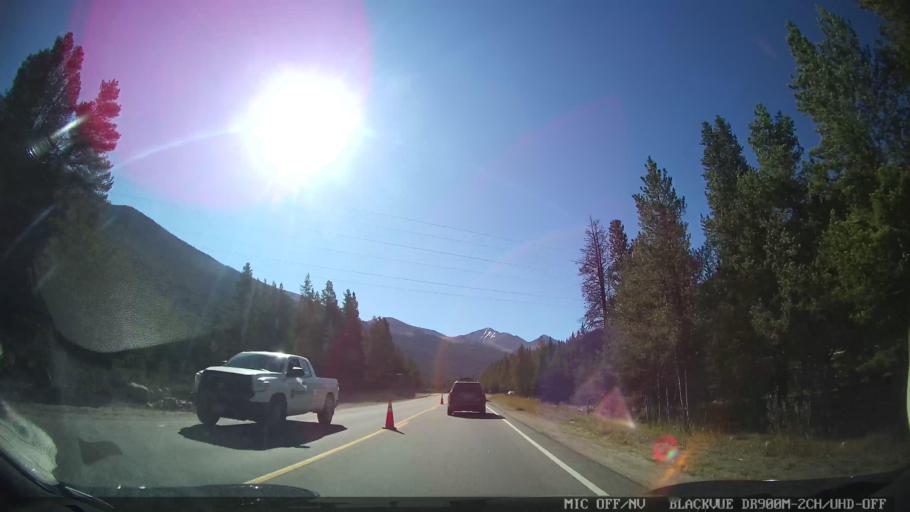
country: US
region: Colorado
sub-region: Summit County
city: Frisco
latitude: 39.4946
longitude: -106.1364
